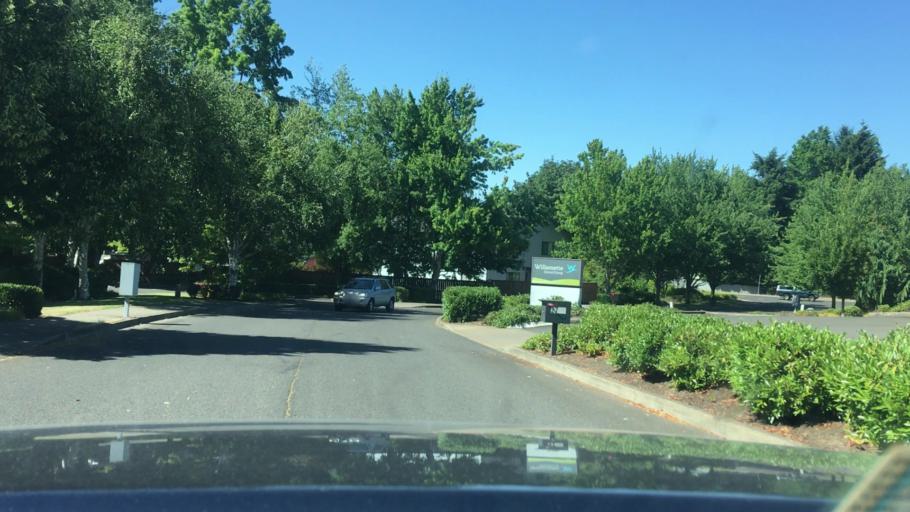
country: US
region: Oregon
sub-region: Lane County
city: Eugene
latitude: 44.0922
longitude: -123.0923
